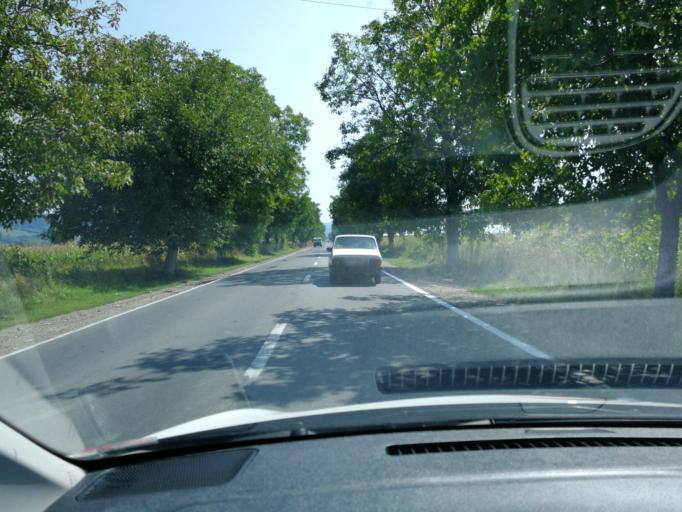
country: RO
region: Prahova
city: Drajna de Jos
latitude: 45.2237
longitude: 26.0322
